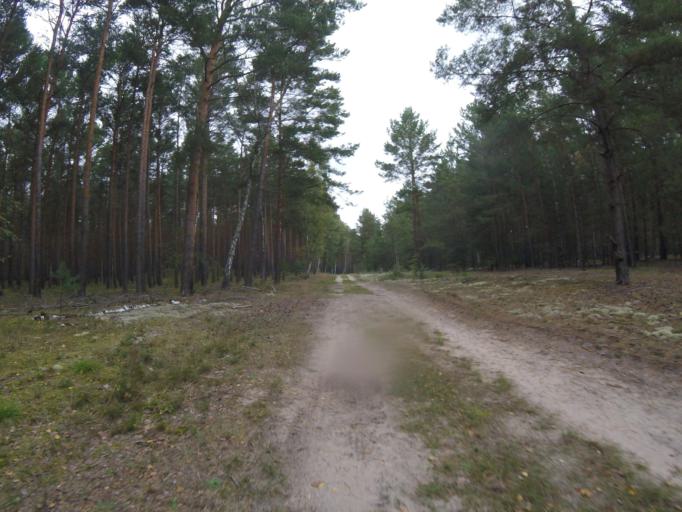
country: DE
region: Brandenburg
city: Gross Koris
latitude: 52.1895
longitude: 13.6749
